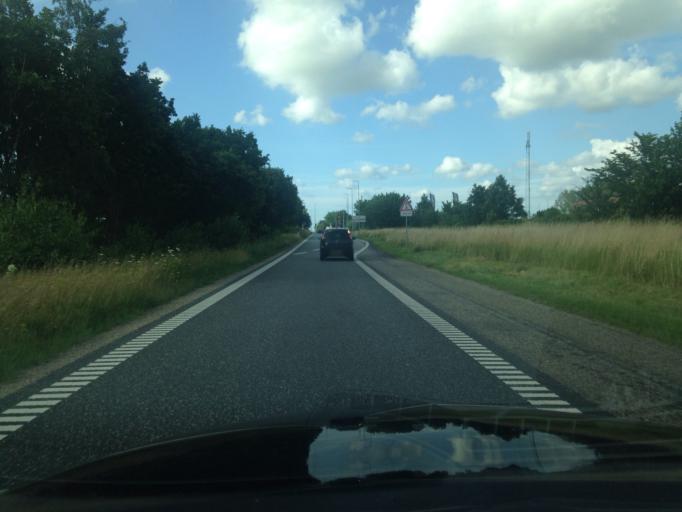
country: DK
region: Capital Region
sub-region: Fredensborg Kommune
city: Kokkedal
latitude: 55.9057
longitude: 12.4728
